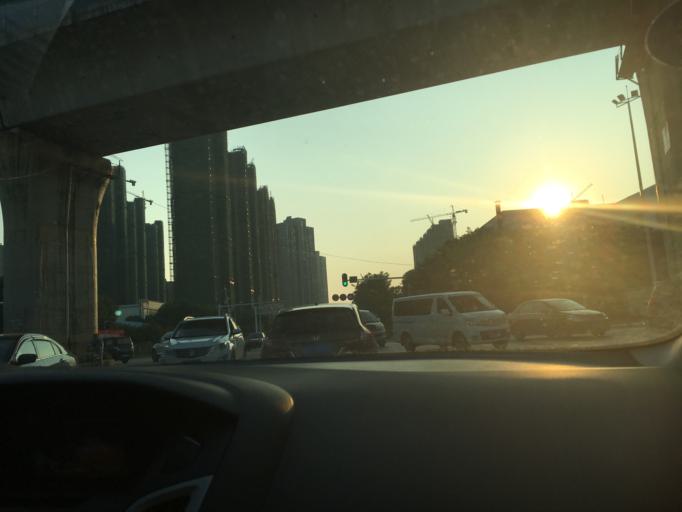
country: CN
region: Hubei
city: Guanshan
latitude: 30.4582
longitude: 114.3834
